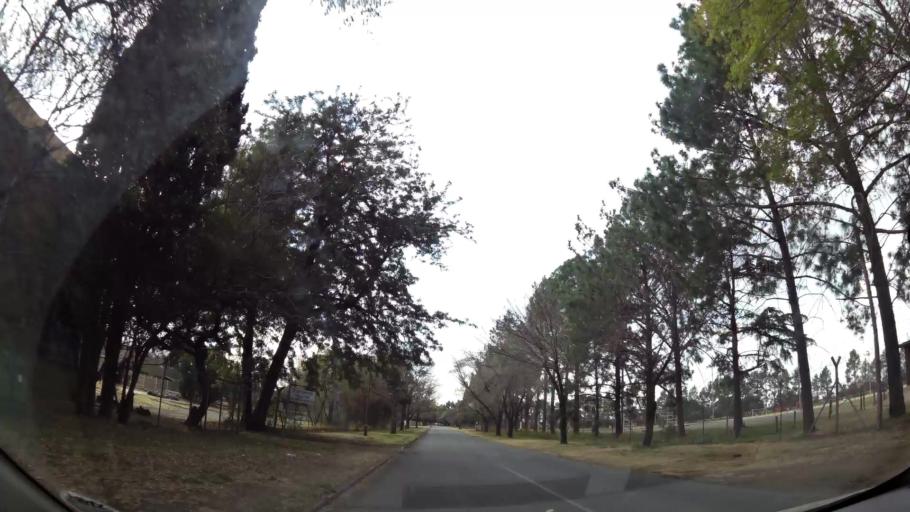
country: ZA
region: Orange Free State
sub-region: Fezile Dabi District Municipality
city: Sasolburg
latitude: -26.8165
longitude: 27.8398
